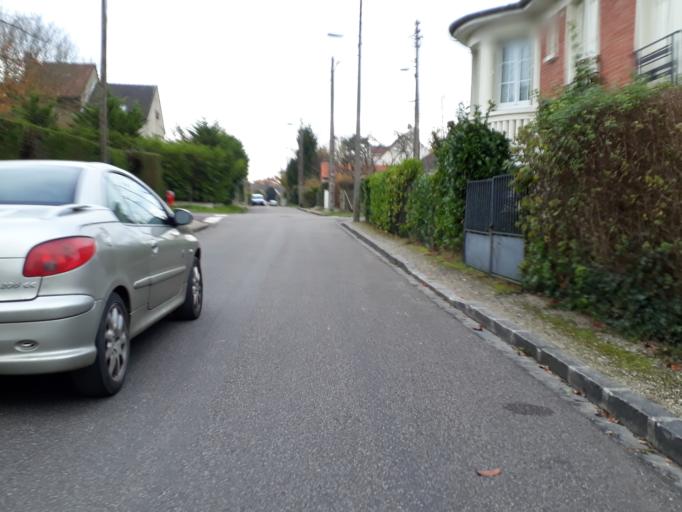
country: FR
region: Ile-de-France
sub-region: Departement de Seine-et-Marne
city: Bois-le-Roi
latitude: 48.4690
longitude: 2.6993
